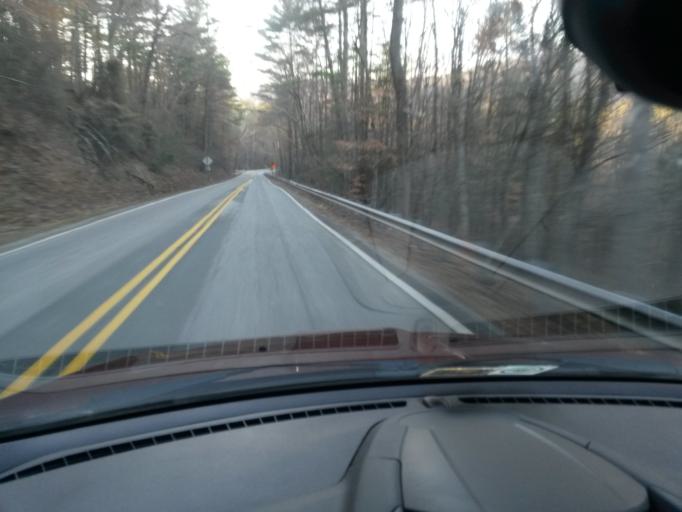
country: US
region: Virginia
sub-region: City of Buena Vista
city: Buena Vista
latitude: 37.7449
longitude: -79.2615
